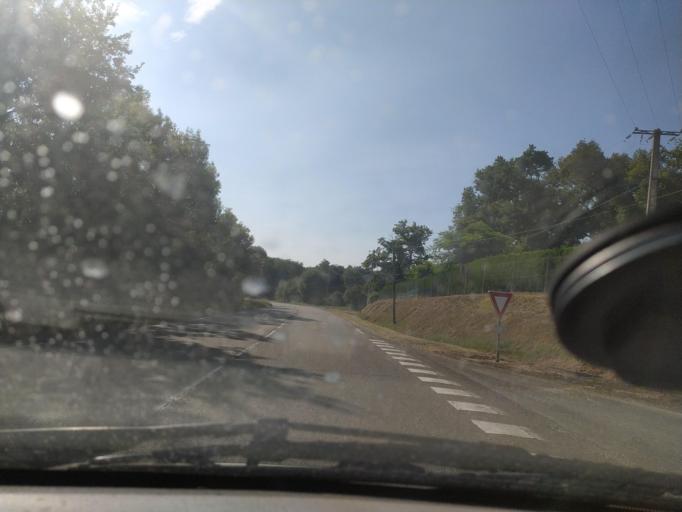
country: FR
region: Midi-Pyrenees
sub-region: Departement du Gers
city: Nogaro
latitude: 43.7885
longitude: 0.0053
